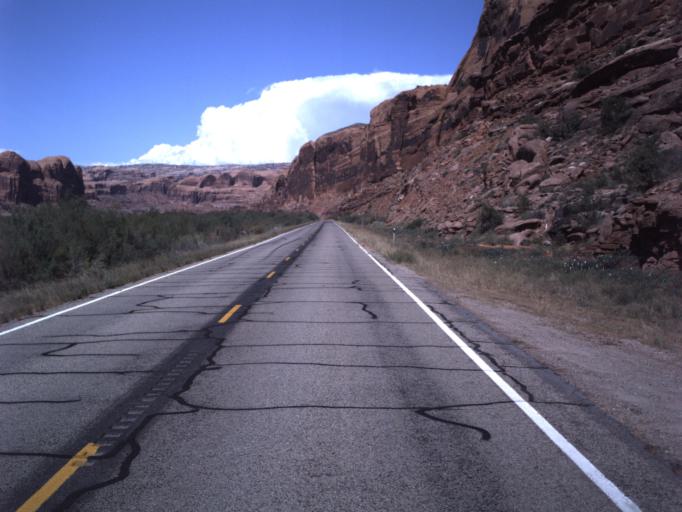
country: US
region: Utah
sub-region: Grand County
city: Moab
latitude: 38.5464
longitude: -109.6318
